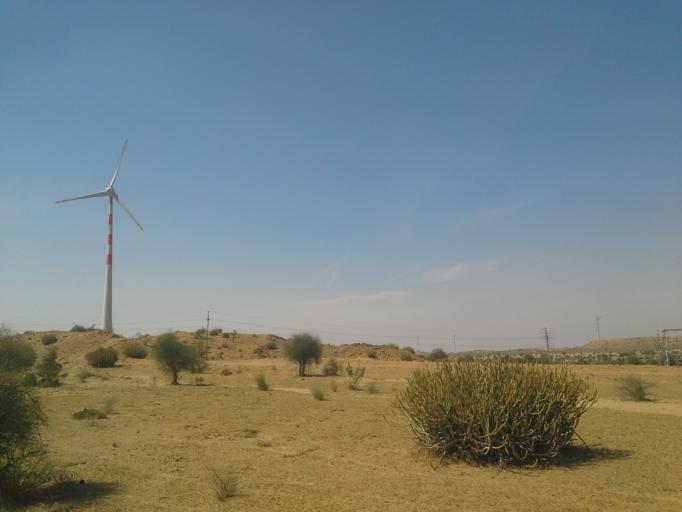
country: IN
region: Rajasthan
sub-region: Jaisalmer
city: Jaisalmer
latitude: 26.6981
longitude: 70.7397
